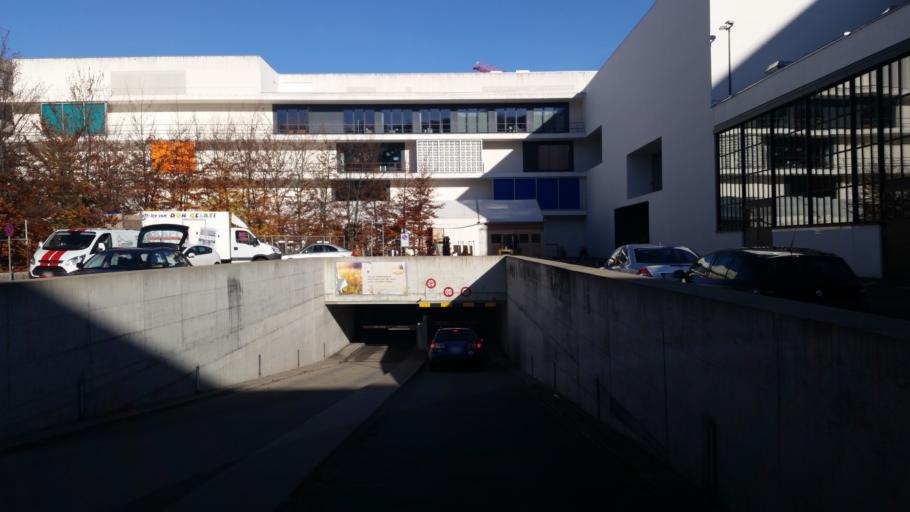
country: CH
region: Aargau
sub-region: Bezirk Baden
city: Baden
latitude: 47.4783
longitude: 8.3042
